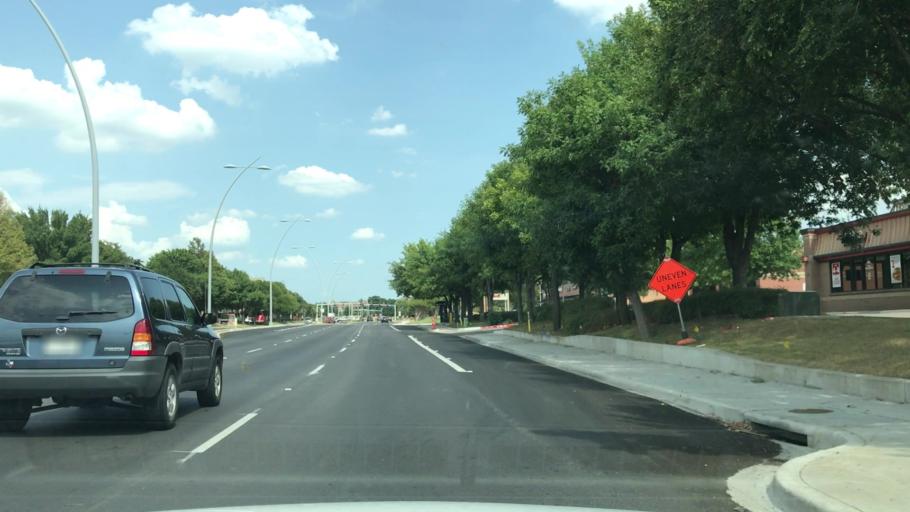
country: US
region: Texas
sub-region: Dallas County
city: Addison
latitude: 32.9531
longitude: -96.8553
